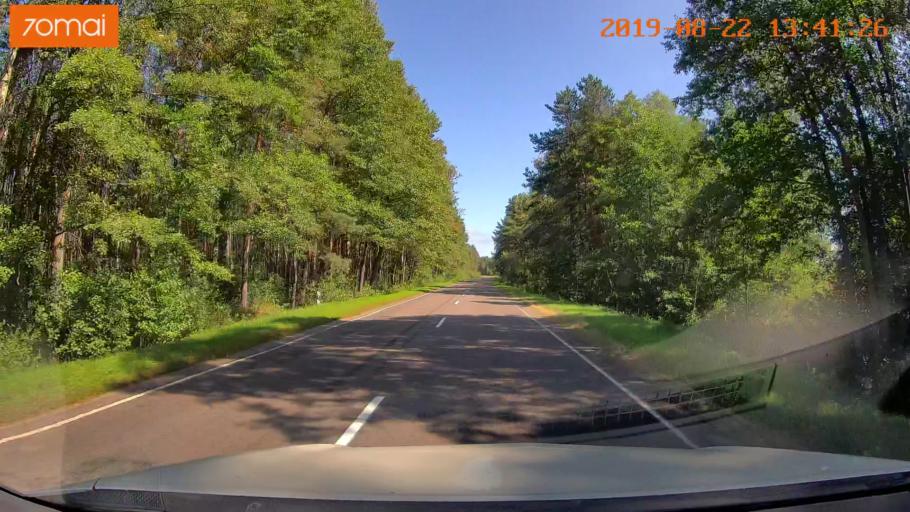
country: BY
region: Minsk
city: Staryya Darohi
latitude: 53.2386
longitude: 28.3971
